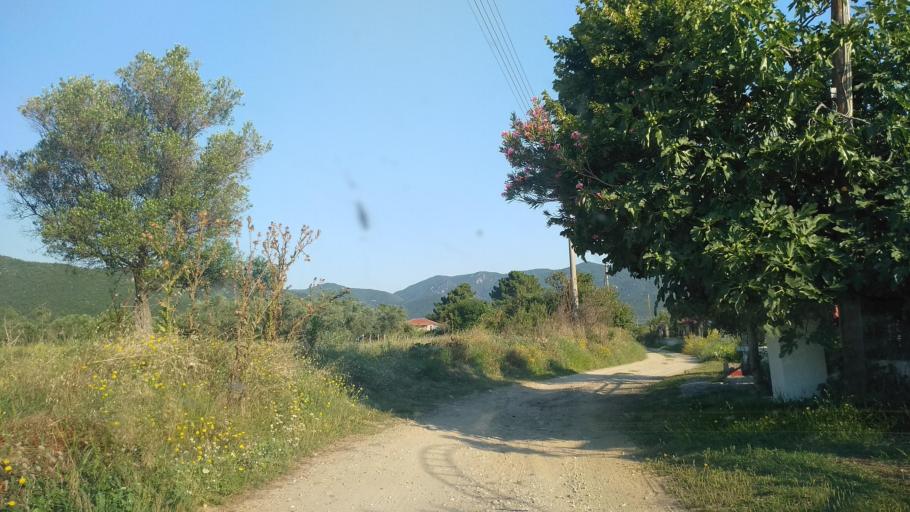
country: GR
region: Central Macedonia
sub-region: Nomos Thessalonikis
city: Nea Vrasna
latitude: 40.6865
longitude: 23.6848
